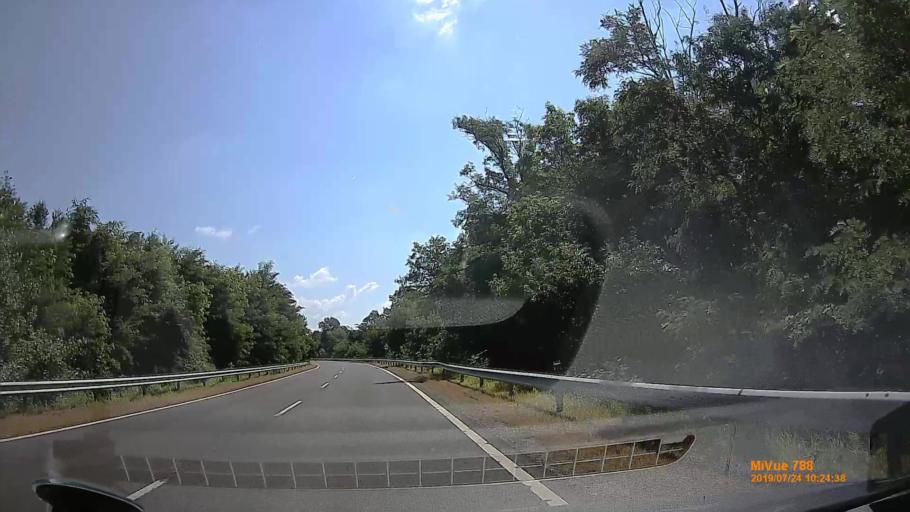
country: HU
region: Szabolcs-Szatmar-Bereg
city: Vasarosnameny
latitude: 48.1507
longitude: 22.3910
